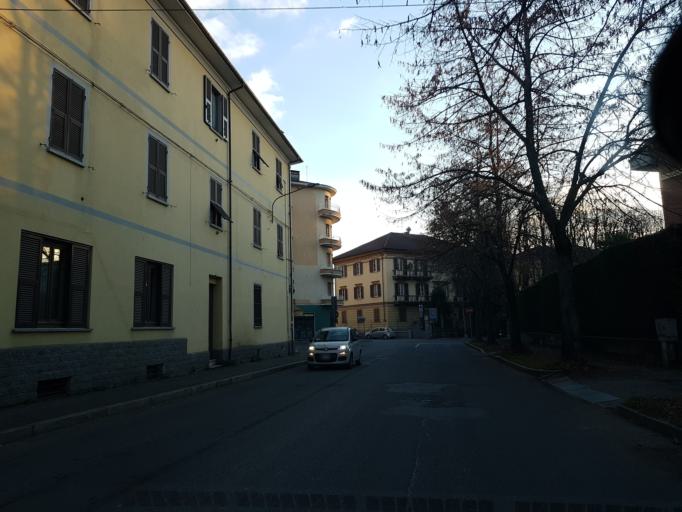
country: IT
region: Piedmont
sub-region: Provincia di Alessandria
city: Novi Ligure
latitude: 44.7636
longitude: 8.7965
